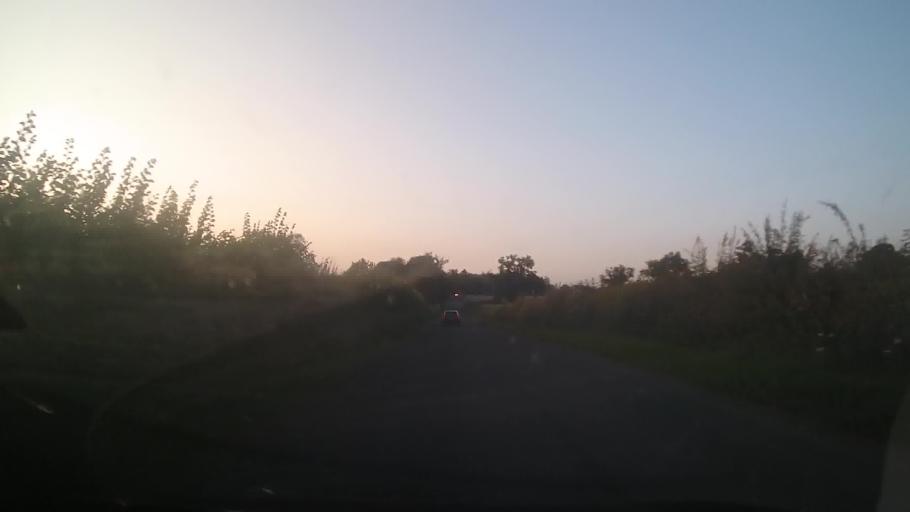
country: GB
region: England
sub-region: Shropshire
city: Bicton
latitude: 52.7639
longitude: -2.7979
